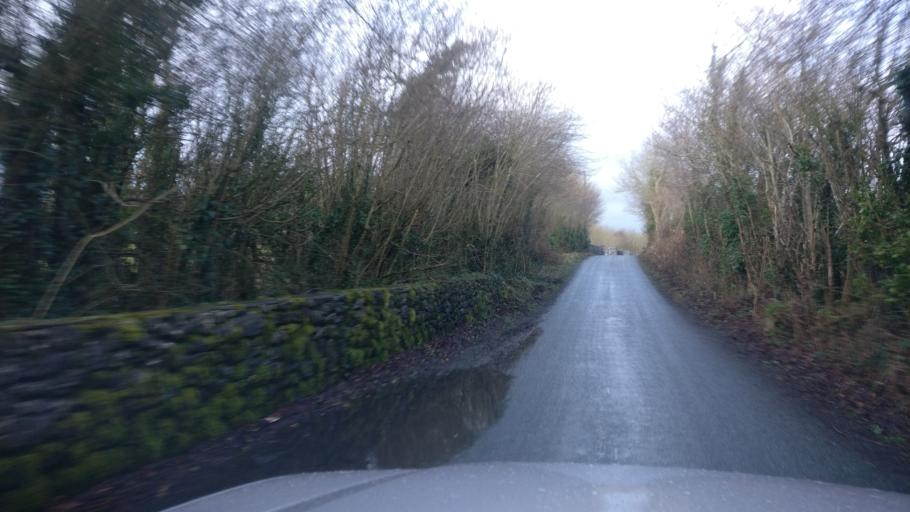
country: IE
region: Connaught
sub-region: County Galway
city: Athenry
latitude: 53.2524
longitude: -8.7218
